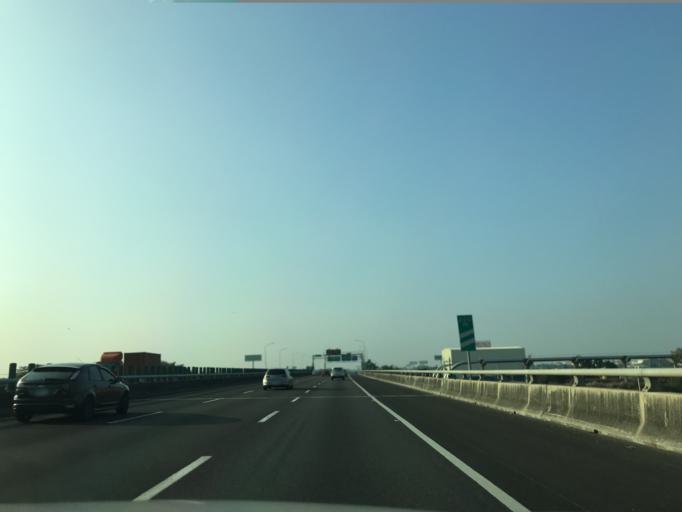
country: TW
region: Taiwan
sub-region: Yunlin
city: Douliu
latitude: 23.7981
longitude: 120.4818
